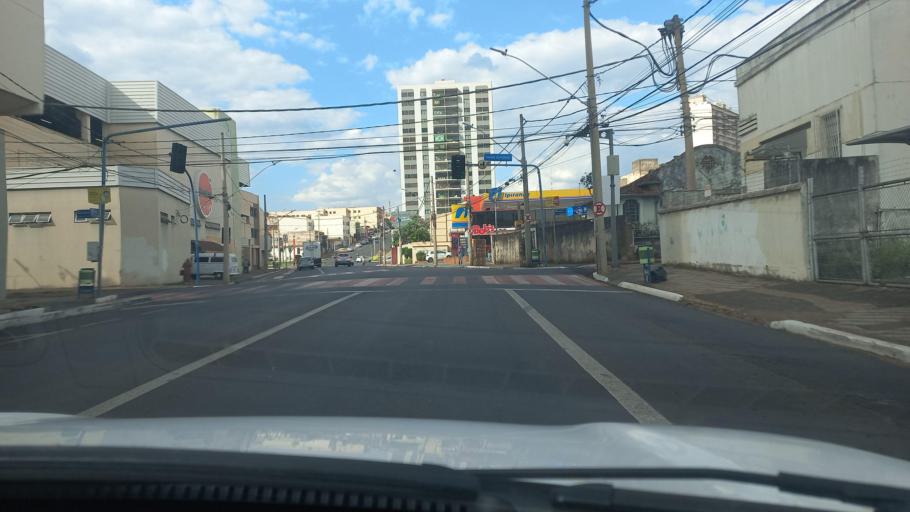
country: BR
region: Minas Gerais
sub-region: Uberaba
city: Uberaba
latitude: -19.7443
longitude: -47.9325
